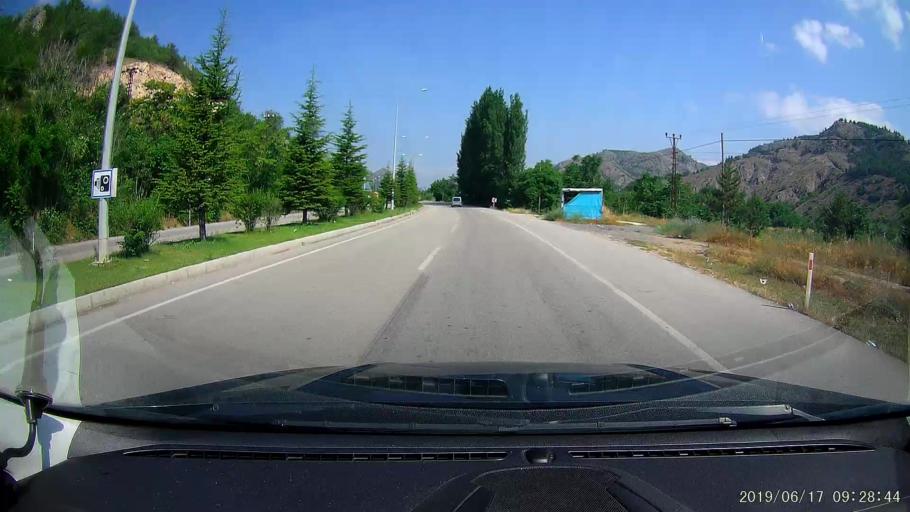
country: TR
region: Amasya
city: Amasya
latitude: 40.6916
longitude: 35.8208
